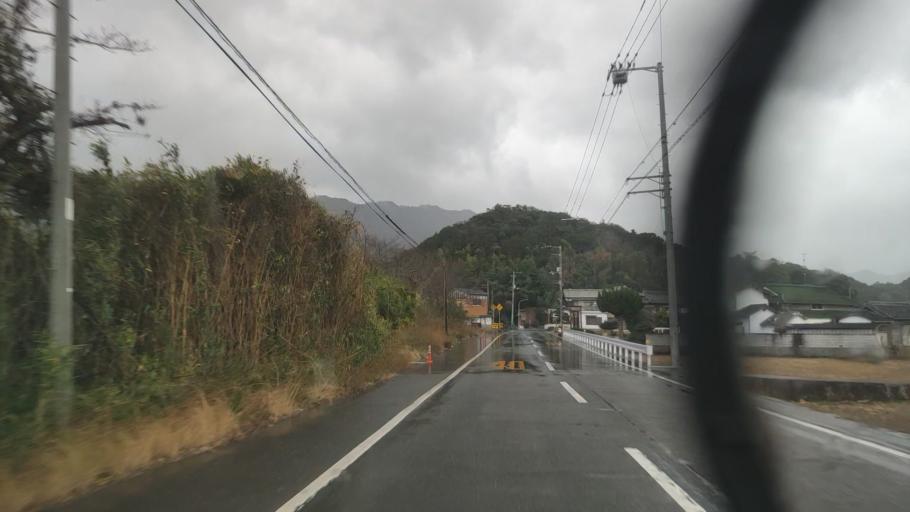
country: JP
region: Tokushima
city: Kamojimacho-jogejima
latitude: 34.2153
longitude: 134.3753
